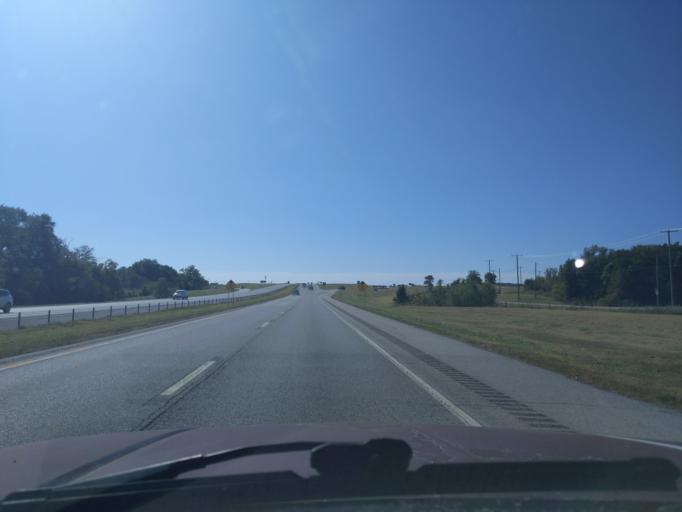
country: US
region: Oklahoma
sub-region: Tulsa County
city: Glenpool
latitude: 35.9939
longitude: -96.0119
